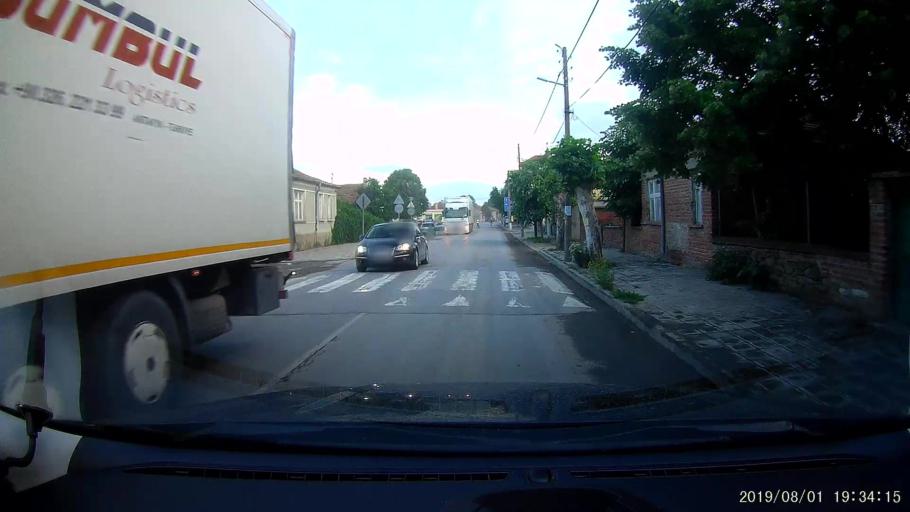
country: BG
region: Burgas
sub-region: Obshtina Sungurlare
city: Sungurlare
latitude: 42.7721
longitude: 26.8782
